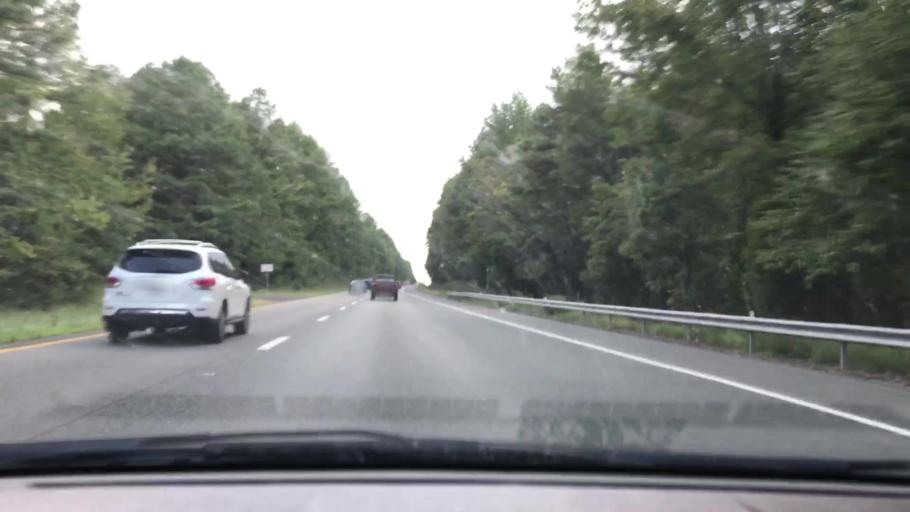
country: US
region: Virginia
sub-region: Goochland County
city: Goochland
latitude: 37.7119
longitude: -77.7883
